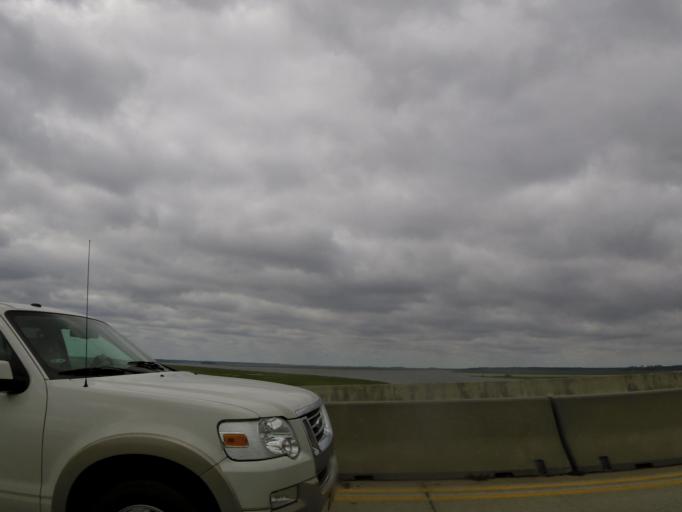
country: US
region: Georgia
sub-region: Glynn County
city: Saint Simon Mills
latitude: 31.1717
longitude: -81.4264
